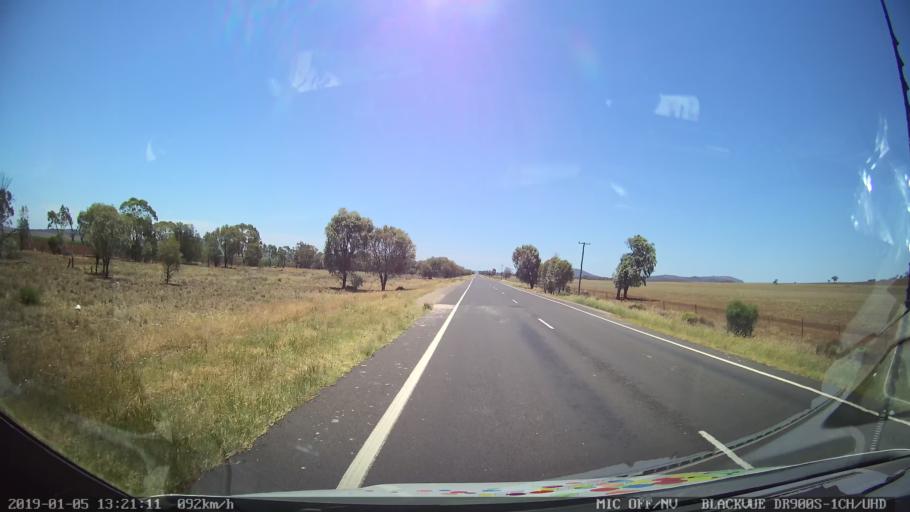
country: AU
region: New South Wales
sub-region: Gunnedah
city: Gunnedah
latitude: -31.0964
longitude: 149.9454
